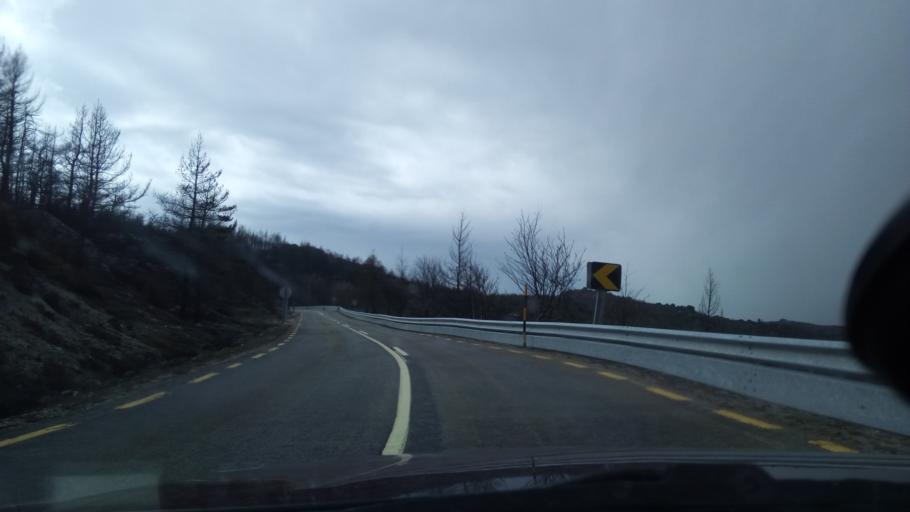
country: PT
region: Guarda
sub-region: Manteigas
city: Manteigas
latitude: 40.4155
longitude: -7.5824
